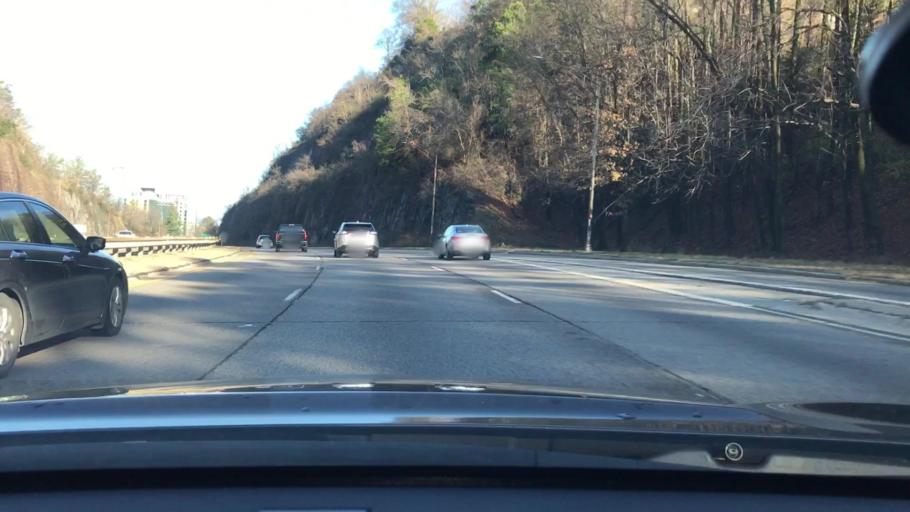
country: US
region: Alabama
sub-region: Jefferson County
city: Homewood
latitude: 33.4934
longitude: -86.7868
